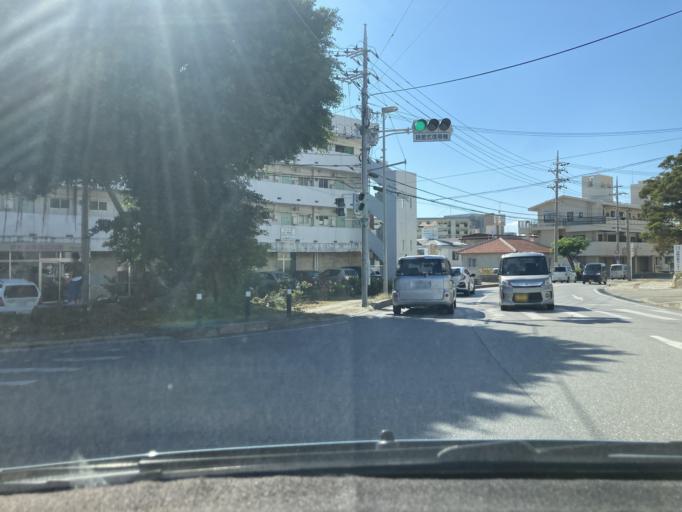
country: JP
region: Okinawa
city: Naha-shi
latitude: 26.2367
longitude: 127.7030
